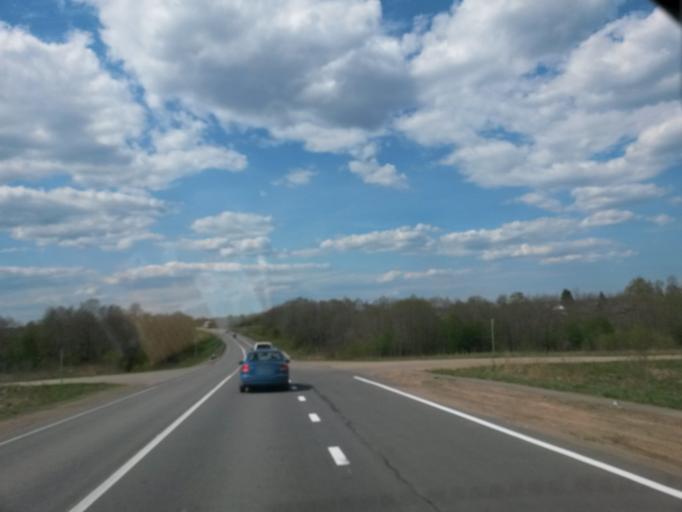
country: RU
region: Jaroslavl
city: Bol'shoye Selo
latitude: 57.7265
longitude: 38.9133
